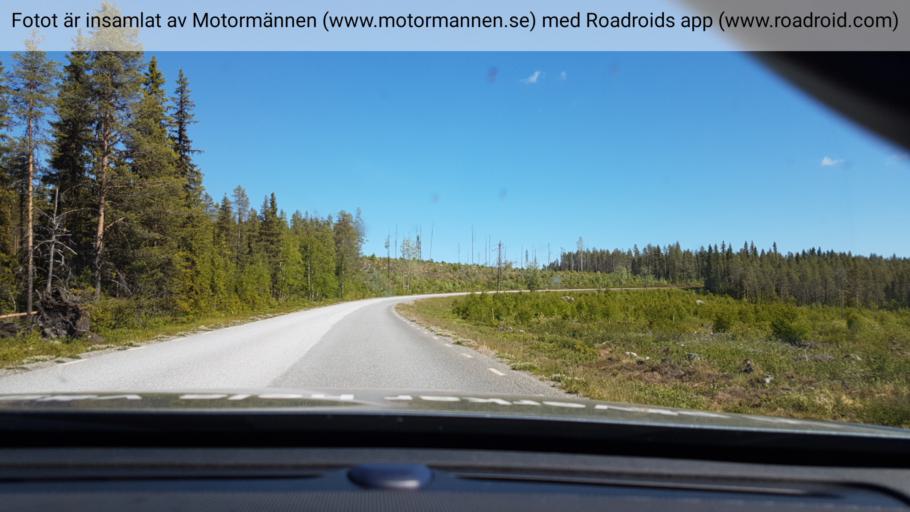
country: SE
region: Vaesterbotten
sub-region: Vilhelmina Kommun
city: Vilhelmina
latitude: 64.6333
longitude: 16.9122
